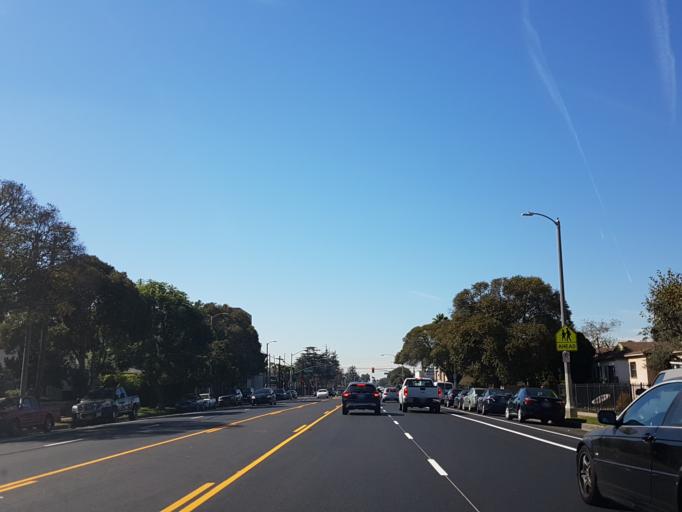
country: US
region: California
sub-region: Los Angeles County
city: Marina del Rey
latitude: 34.0014
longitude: -118.4264
